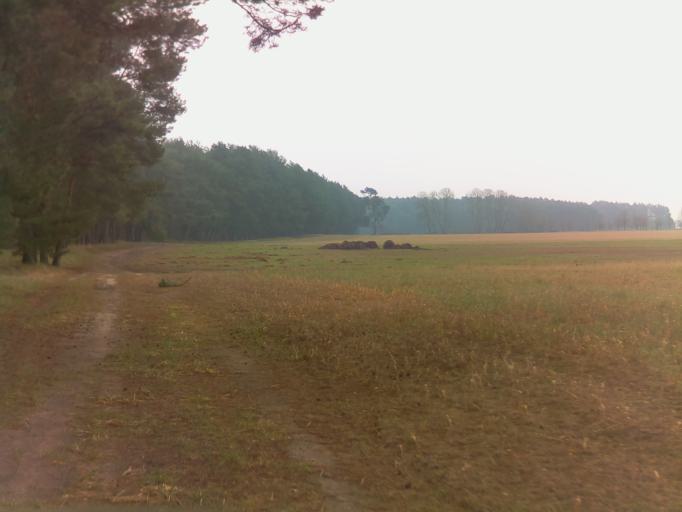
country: DE
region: Brandenburg
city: Neu Zauche
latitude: 51.9700
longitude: 14.1095
